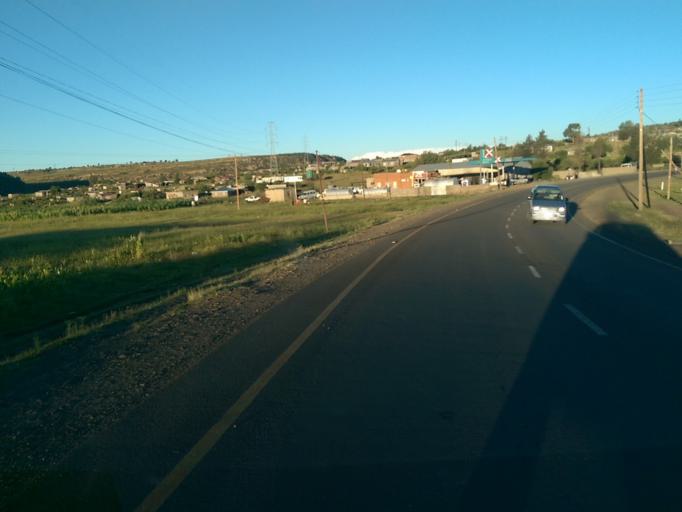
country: LS
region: Maseru
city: Maseru
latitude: -29.4035
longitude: 27.5636
